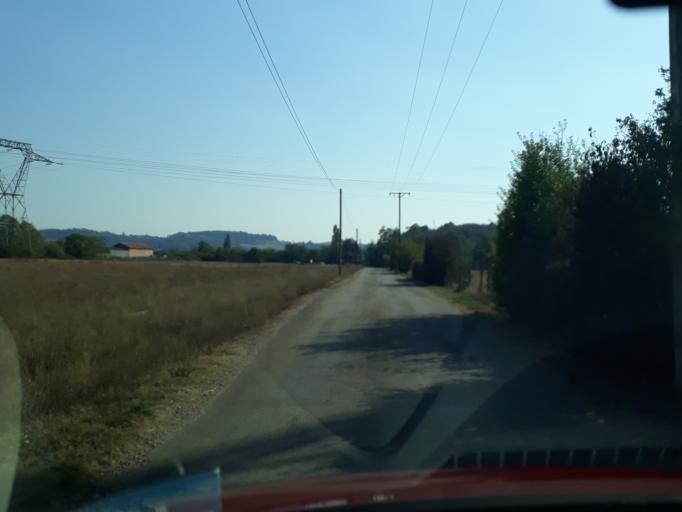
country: FR
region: Rhone-Alpes
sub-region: Departement du Rhone
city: Toussieu
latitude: 45.6674
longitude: 4.9943
